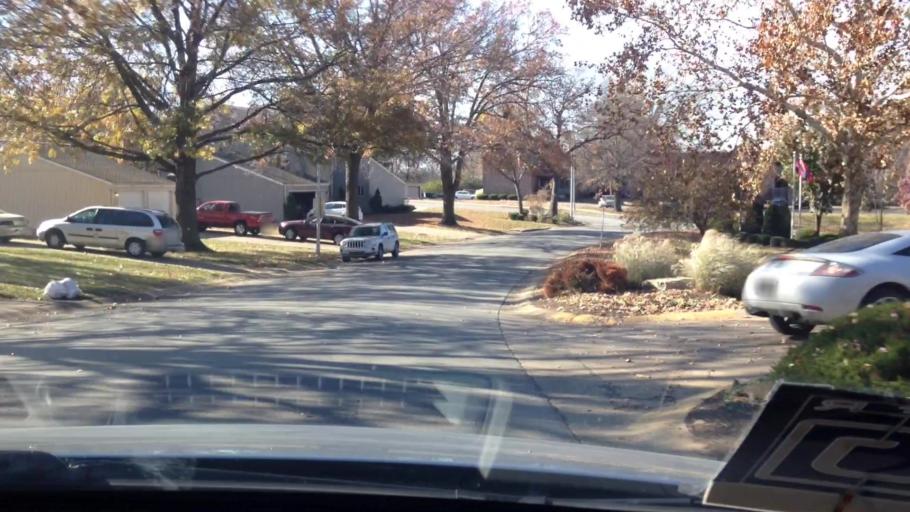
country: US
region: Kansas
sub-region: Johnson County
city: Leawood
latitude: 38.9515
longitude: -94.5705
